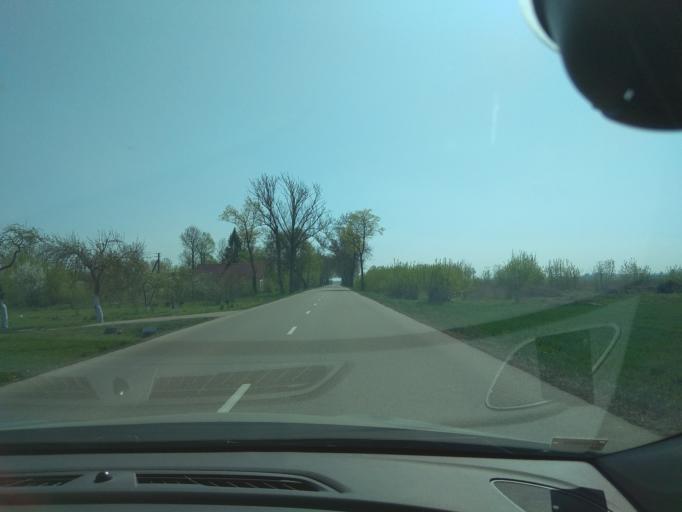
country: LT
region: Panevezys
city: Pasvalys
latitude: 55.9489
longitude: 24.2129
